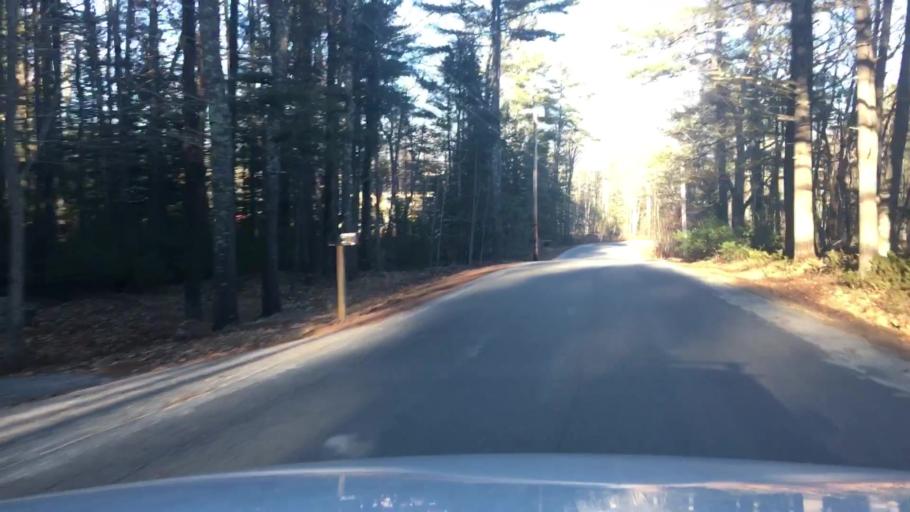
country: US
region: Maine
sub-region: Cumberland County
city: Brunswick
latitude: 43.8853
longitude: -69.9157
